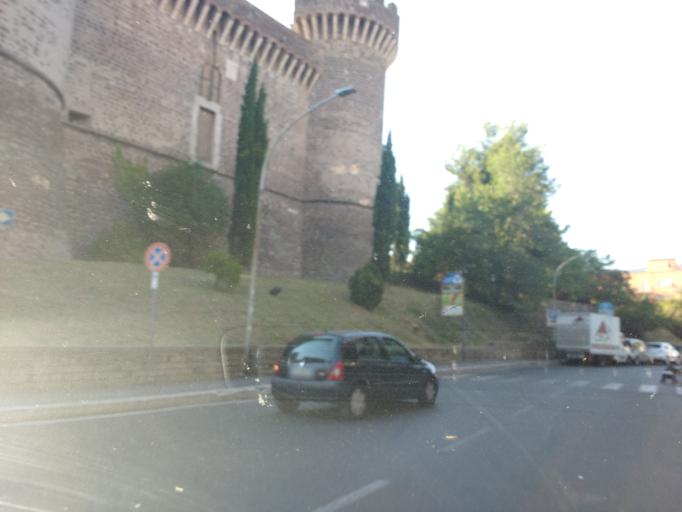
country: IT
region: Latium
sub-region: Citta metropolitana di Roma Capitale
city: Tivoli
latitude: 41.9598
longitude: 12.7986
